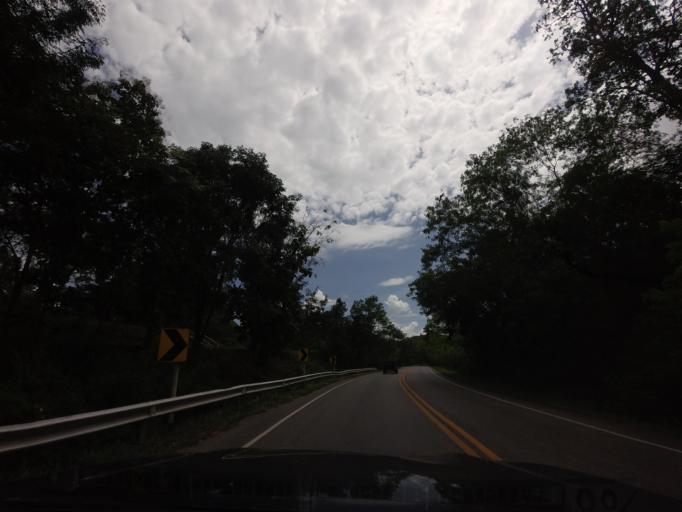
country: TH
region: Nong Khai
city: Pho Tak
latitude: 17.8035
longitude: 102.3191
